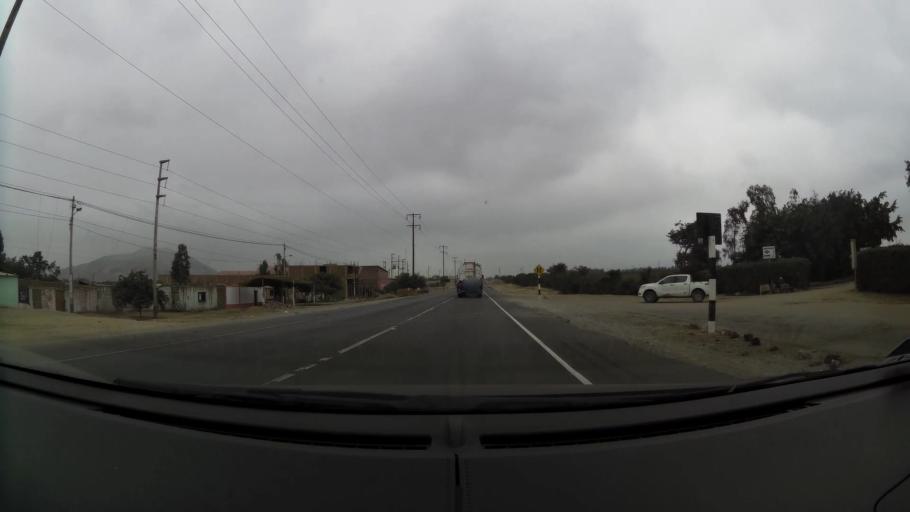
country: PE
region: La Libertad
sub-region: Viru
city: Viru
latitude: -8.4555
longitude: -78.7286
